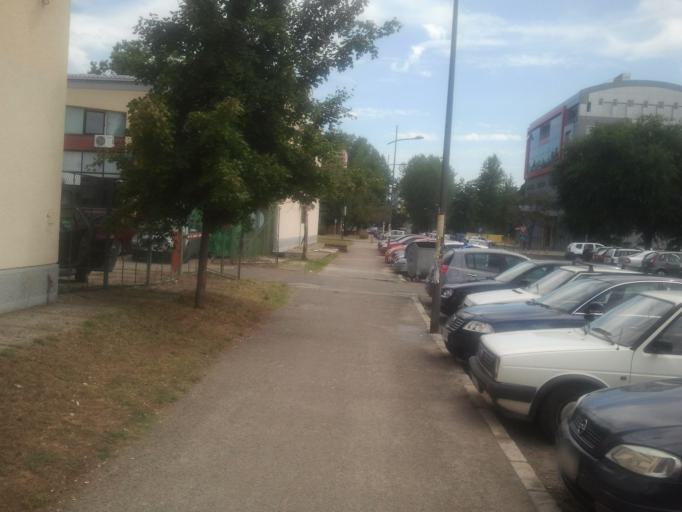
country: RS
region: Autonomna Pokrajina Vojvodina
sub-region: Juznobacki Okrug
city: Novi Sad
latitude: 45.2456
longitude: 19.8500
